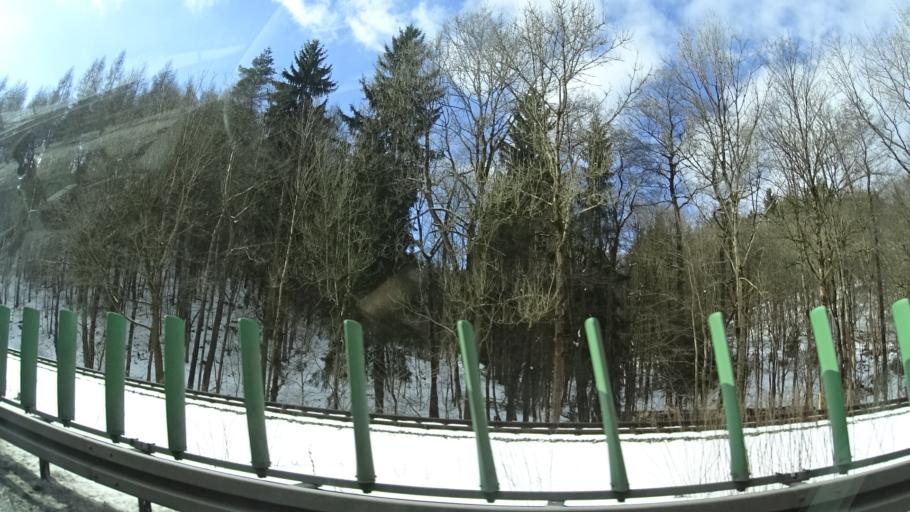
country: DE
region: Thuringia
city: Suhl
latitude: 50.6313
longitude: 10.6966
